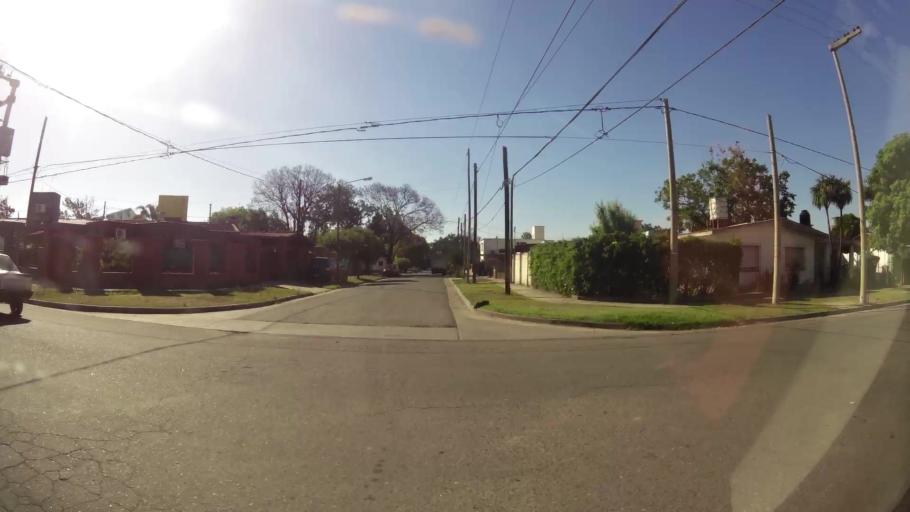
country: AR
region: Cordoba
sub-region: Departamento de Capital
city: Cordoba
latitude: -31.3612
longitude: -64.2023
